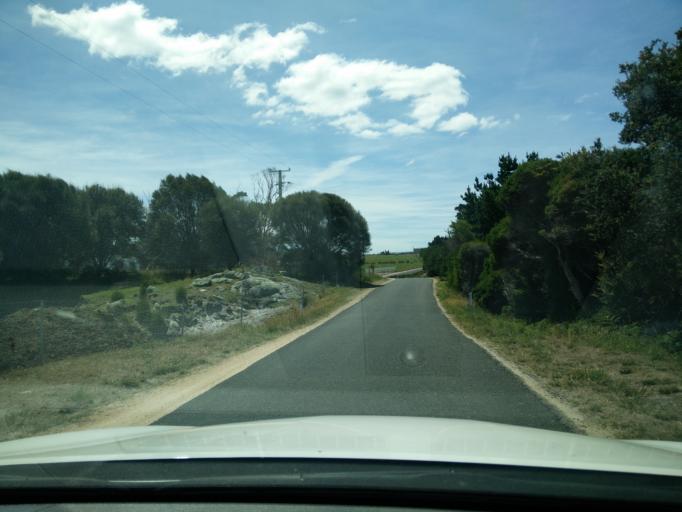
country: AU
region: Tasmania
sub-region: Break O'Day
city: St Helens
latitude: -41.1715
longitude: 148.2796
